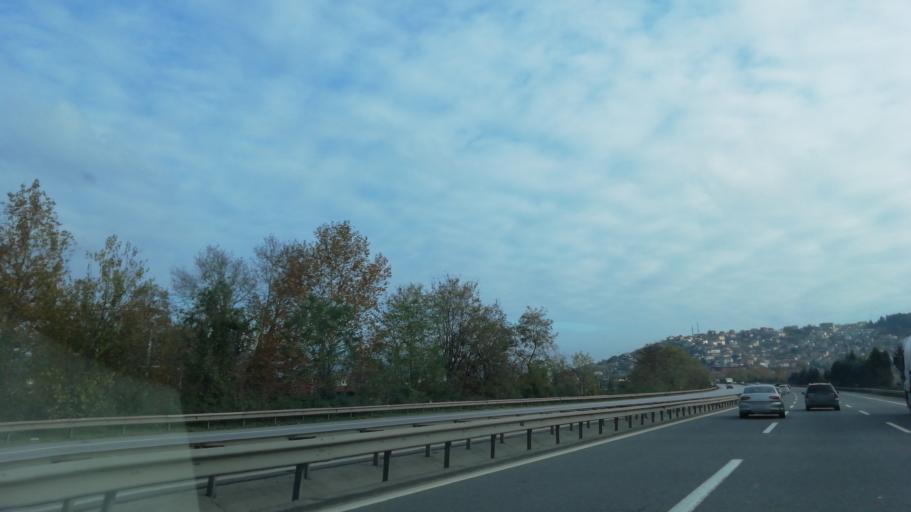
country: TR
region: Sakarya
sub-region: Merkez
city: Sapanca
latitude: 40.6876
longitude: 30.2753
